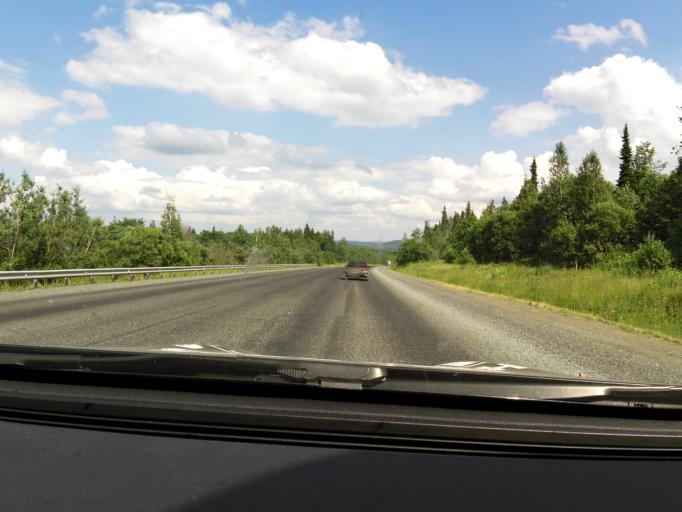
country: RU
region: Sverdlovsk
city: Arti
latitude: 56.7885
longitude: 58.5602
